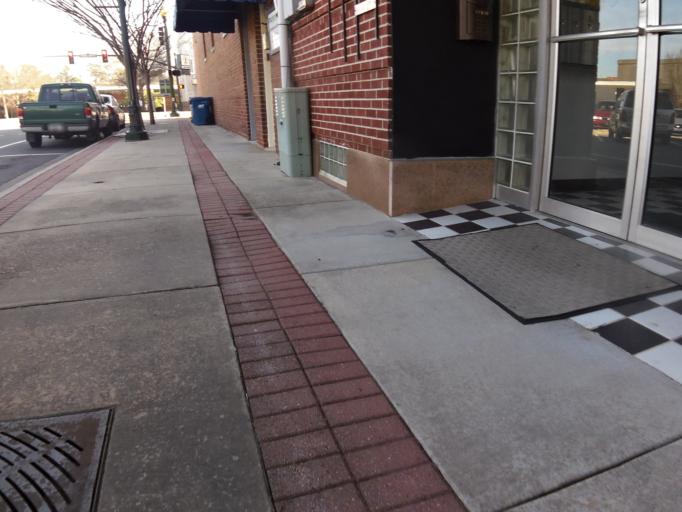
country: US
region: Georgia
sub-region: Whitfield County
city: Dalton
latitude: 34.7722
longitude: -84.9684
